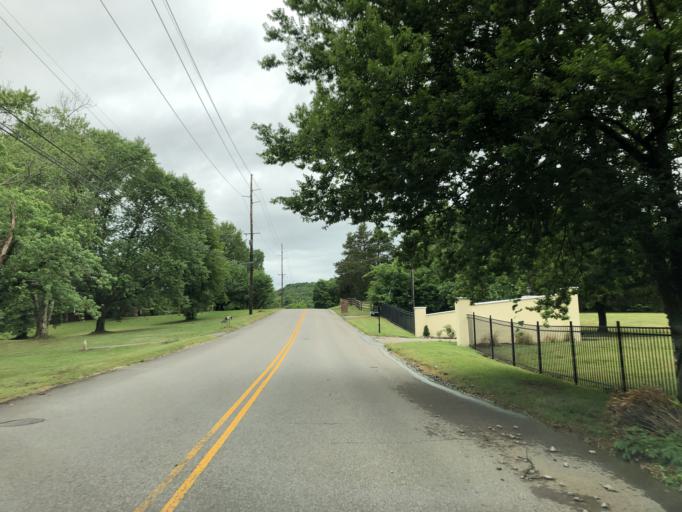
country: US
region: Tennessee
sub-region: Davidson County
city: Goodlettsville
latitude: 36.2699
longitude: -86.7714
